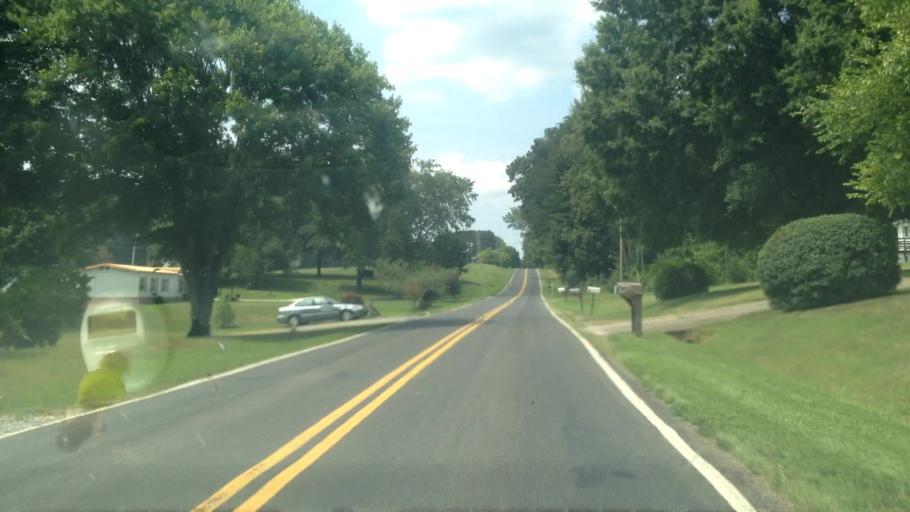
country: US
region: North Carolina
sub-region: Forsyth County
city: Walkertown
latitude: 36.2175
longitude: -80.1144
